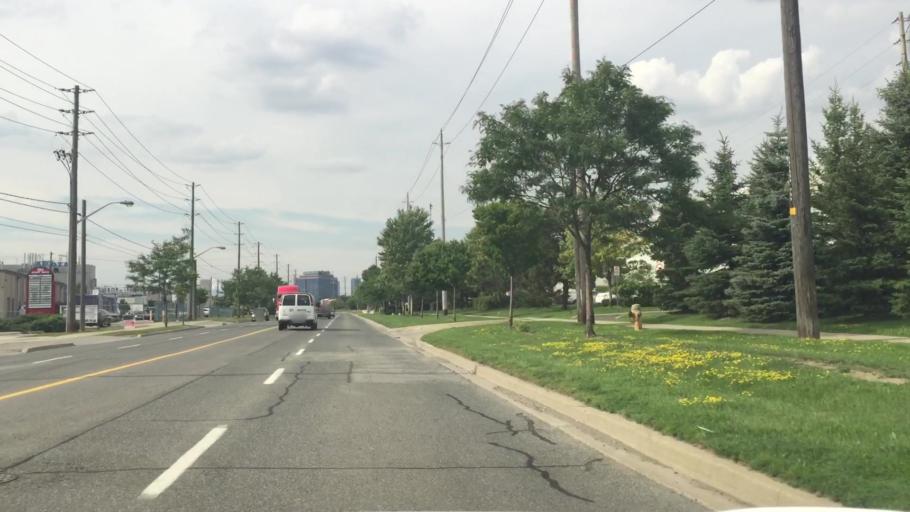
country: CA
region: Ontario
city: Concord
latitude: 43.7611
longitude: -79.5397
